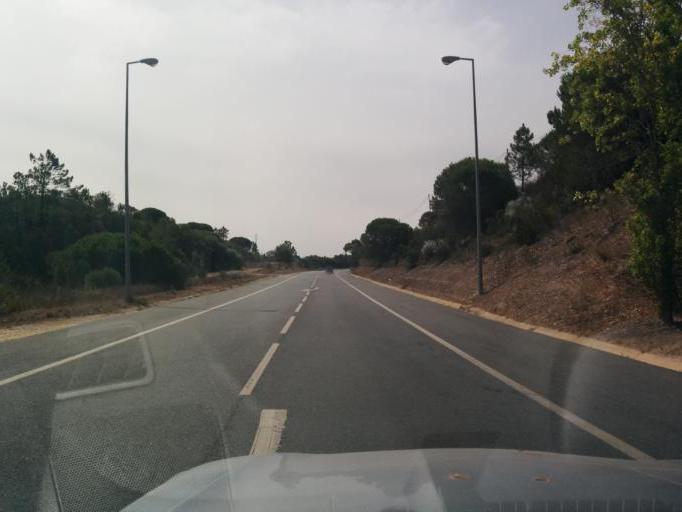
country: PT
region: Beja
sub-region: Odemira
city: Vila Nova de Milfontes
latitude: 37.7247
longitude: -8.7689
